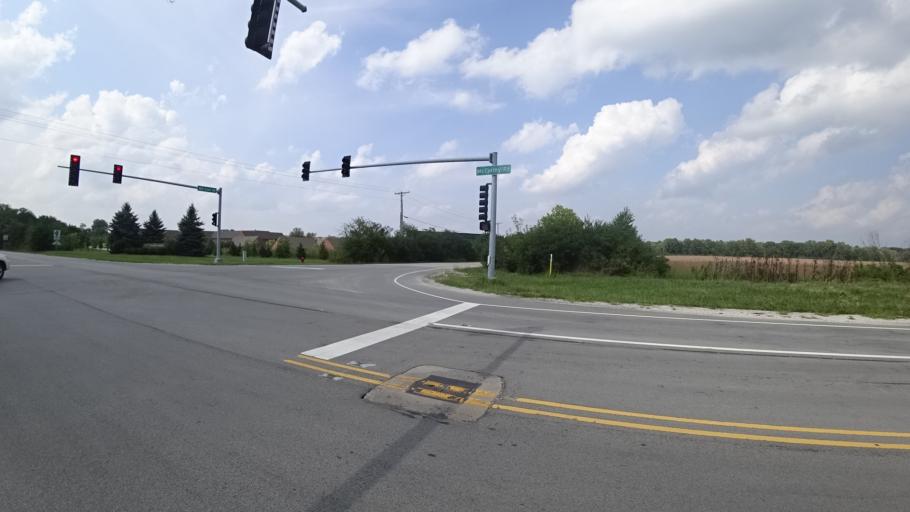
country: US
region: Illinois
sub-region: Will County
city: Goodings Grove
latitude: 41.6657
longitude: -87.9125
